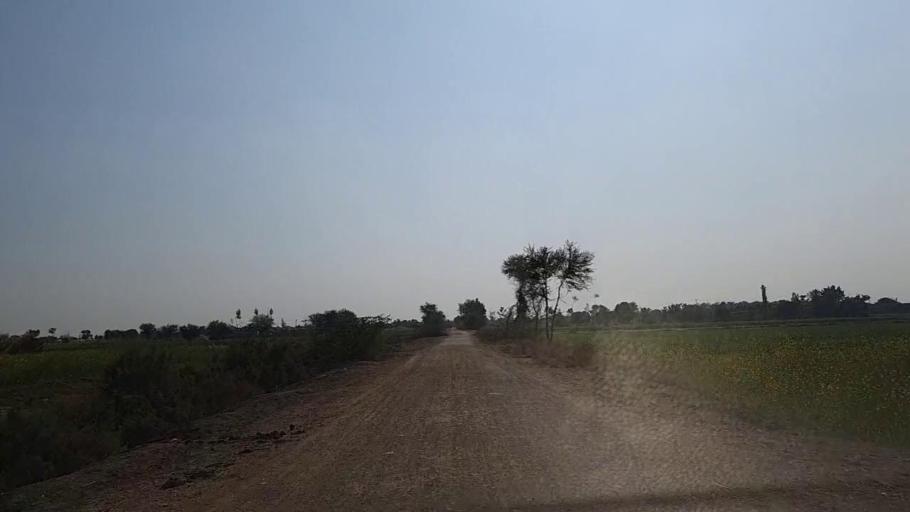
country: PK
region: Sindh
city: Jam Sahib
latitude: 26.2678
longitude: 68.5288
